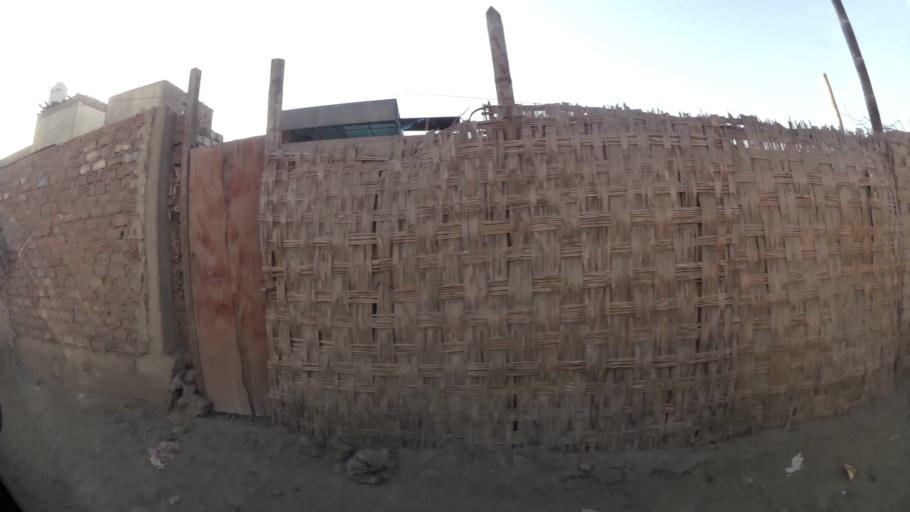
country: PE
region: Ica
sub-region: Provincia de Ica
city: Ica
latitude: -14.0579
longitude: -75.7288
